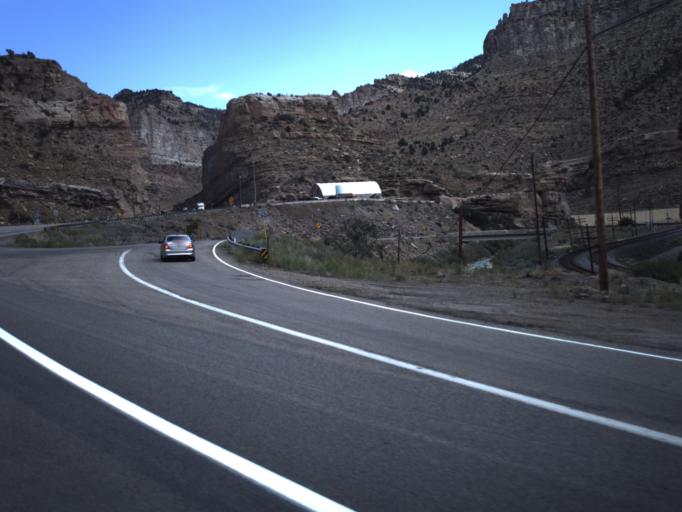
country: US
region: Utah
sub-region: Carbon County
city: Helper
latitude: 39.7246
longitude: -110.8672
